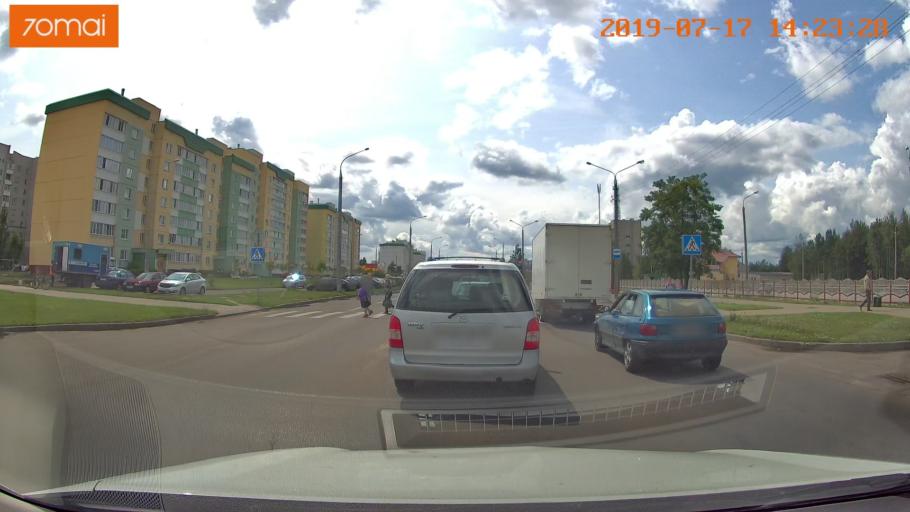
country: BY
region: Mogilev
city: Babruysk
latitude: 53.1700
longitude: 29.1717
